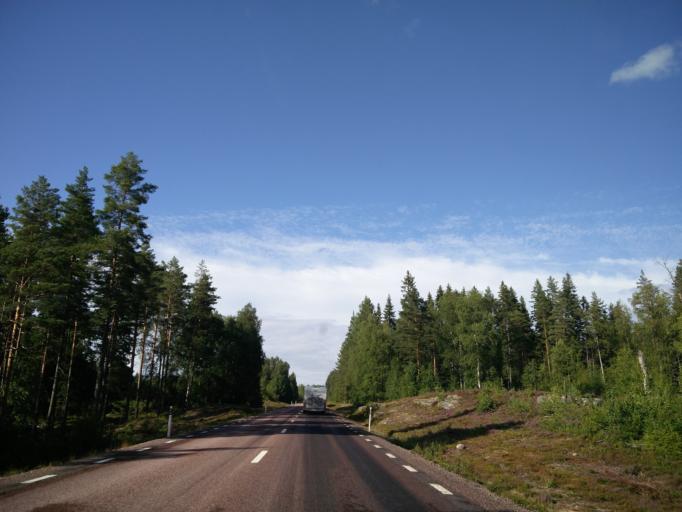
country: SE
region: Vaermland
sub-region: Hagfors Kommun
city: Ekshaerad
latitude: 60.4717
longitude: 13.3038
